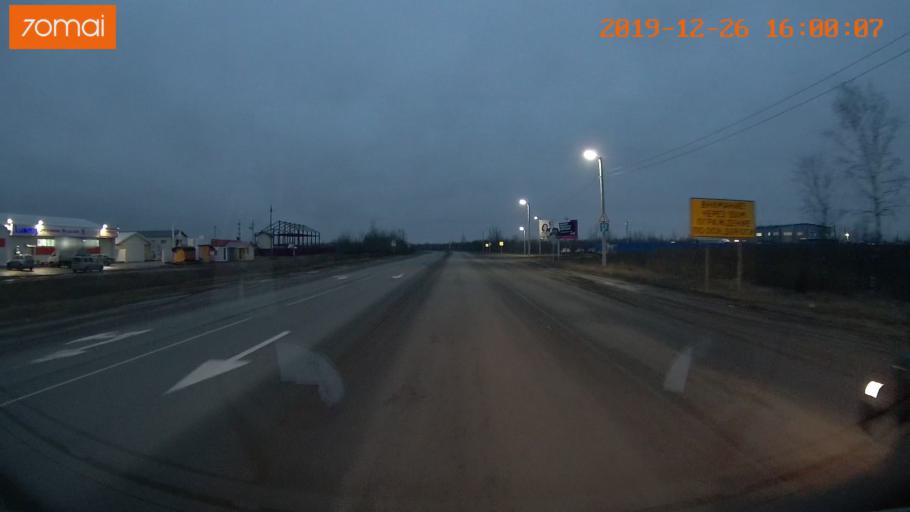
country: RU
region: Jaroslavl
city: Rybinsk
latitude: 58.0275
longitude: 38.8035
